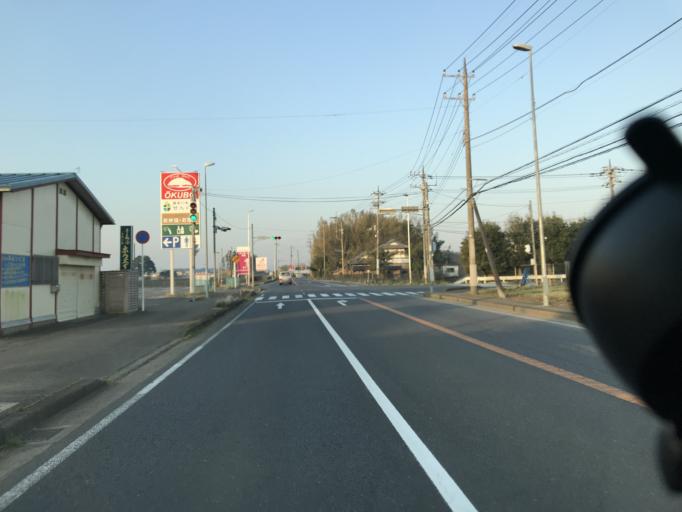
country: JP
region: Chiba
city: Narita
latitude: 35.8189
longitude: 140.4044
